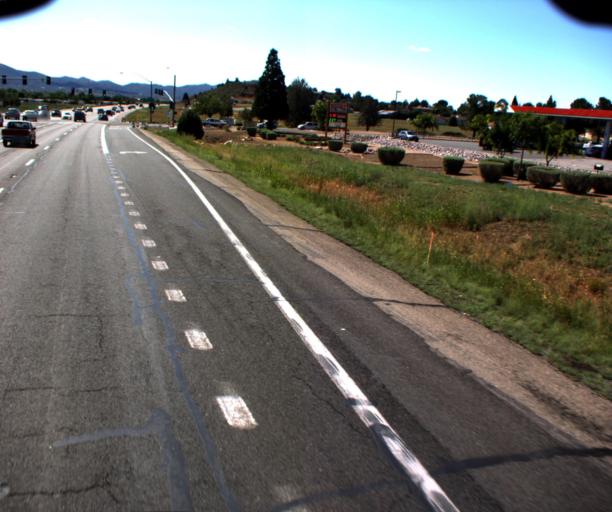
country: US
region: Arizona
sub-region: Yavapai County
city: Dewey-Humboldt
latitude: 34.5626
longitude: -112.2607
